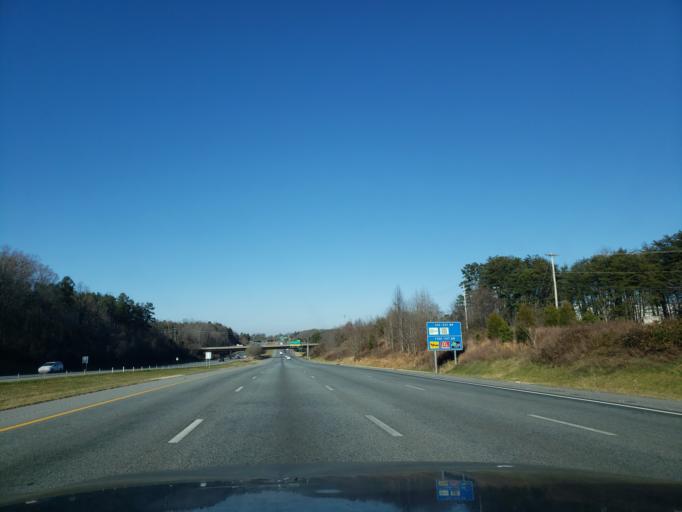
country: US
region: North Carolina
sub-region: Guilford County
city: High Point
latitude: 35.9702
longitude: -79.9747
